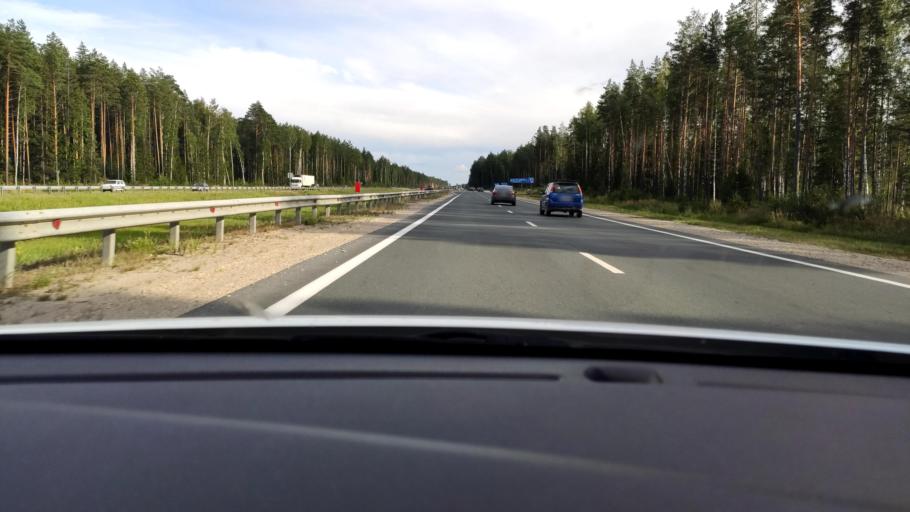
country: RU
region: Mariy-El
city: Surok
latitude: 56.5292
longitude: 48.0030
